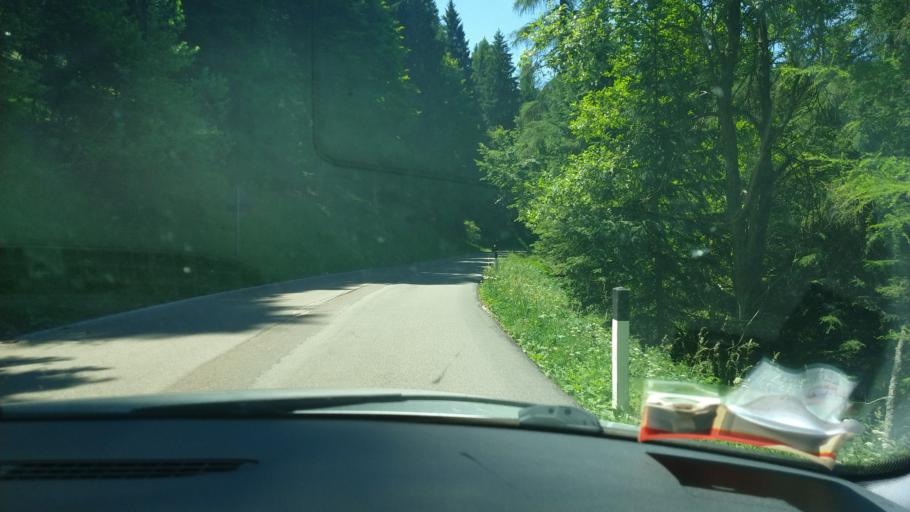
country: IT
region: Veneto
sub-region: Provincia di Vicenza
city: Lastebasse
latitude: 45.9087
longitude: 11.2251
